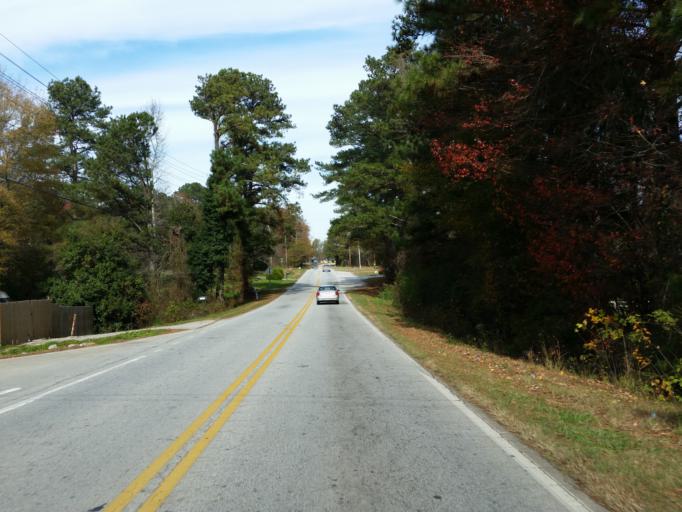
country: US
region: Georgia
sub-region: Douglas County
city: Lithia Springs
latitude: 33.7356
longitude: -84.6671
